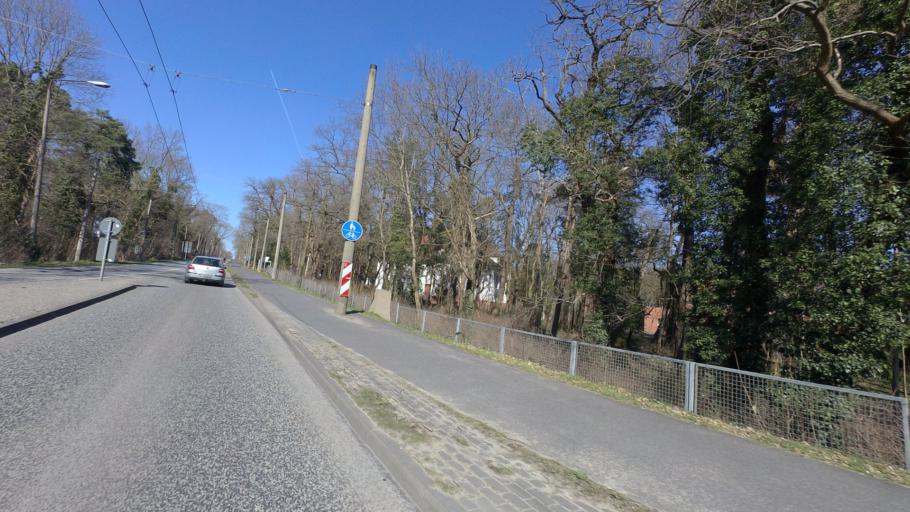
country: DE
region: Brandenburg
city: Eberswalde
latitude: 52.8435
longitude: 13.8220
